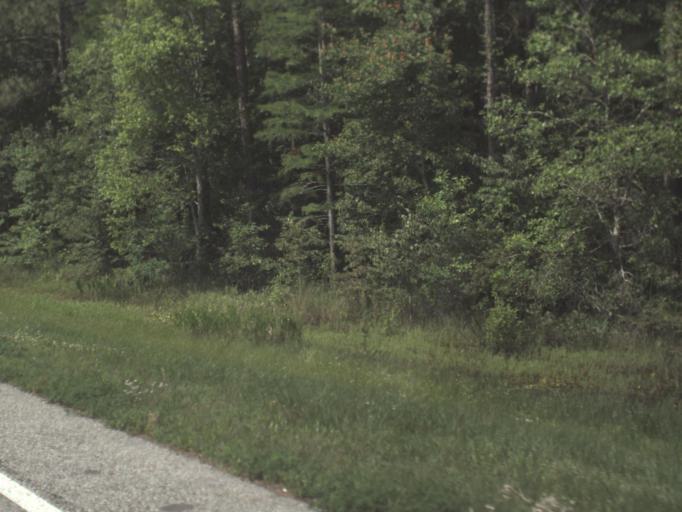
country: US
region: Florida
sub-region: Saint Johns County
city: Butler Beach
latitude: 29.7178
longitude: -81.3037
